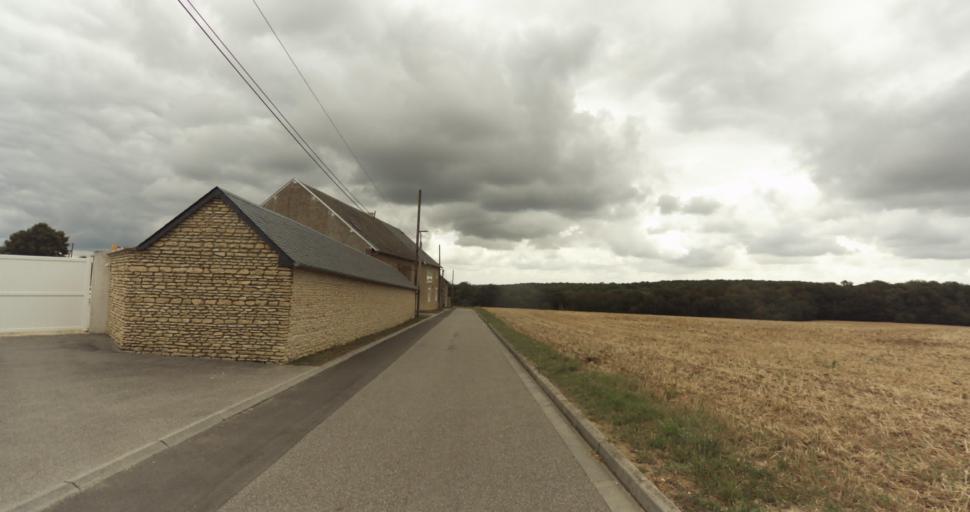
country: FR
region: Haute-Normandie
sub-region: Departement de l'Eure
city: Menilles
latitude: 49.0248
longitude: 1.3072
